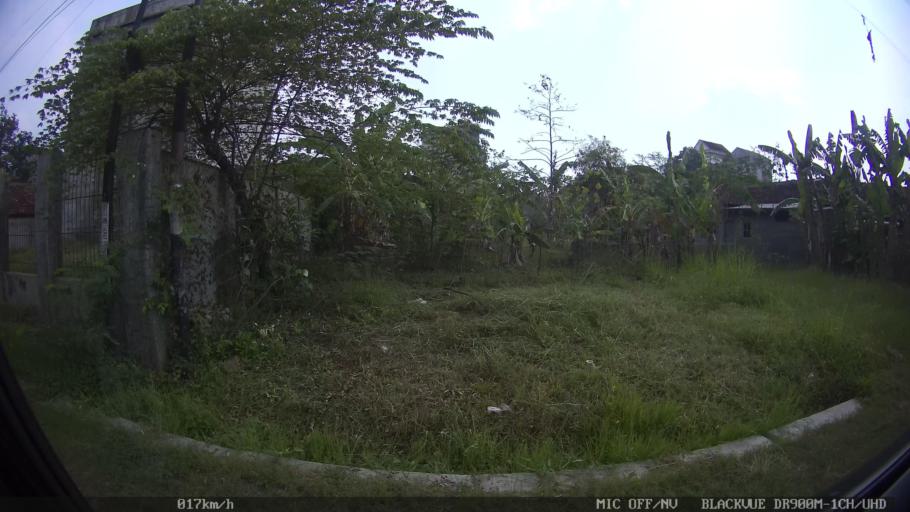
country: ID
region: Lampung
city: Gadingrejo
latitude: -5.3715
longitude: 105.0626
